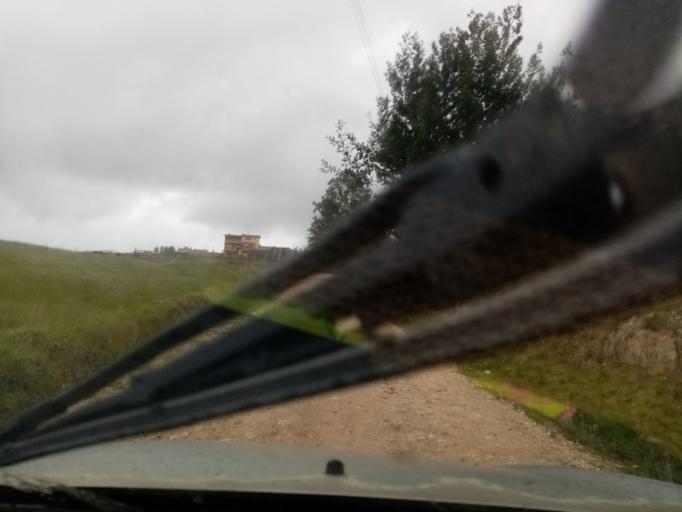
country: CO
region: Boyaca
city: Siachoque
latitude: 5.5593
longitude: -73.2502
